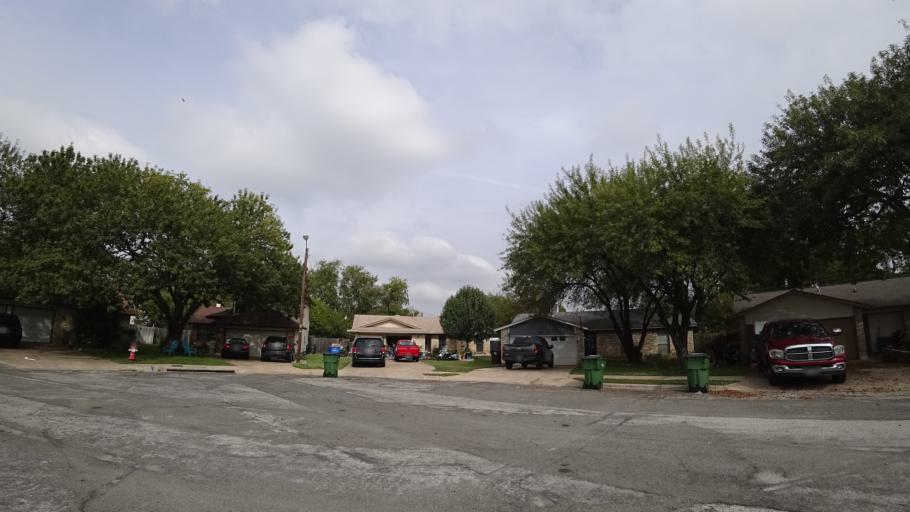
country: US
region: Texas
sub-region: Williamson County
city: Round Rock
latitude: 30.4925
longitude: -97.6909
